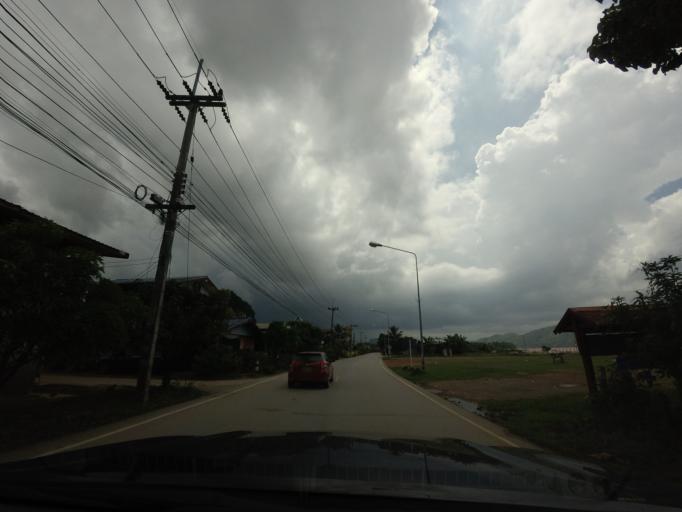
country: LA
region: Vientiane
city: Muang Sanakham
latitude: 18.0006
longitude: 101.7558
